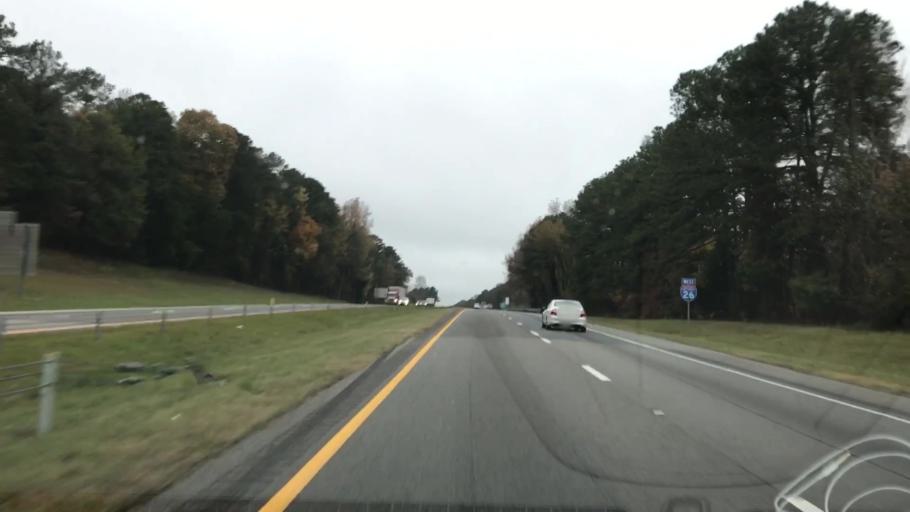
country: US
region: South Carolina
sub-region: Newberry County
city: Newberry
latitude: 34.2983
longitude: -81.5530
